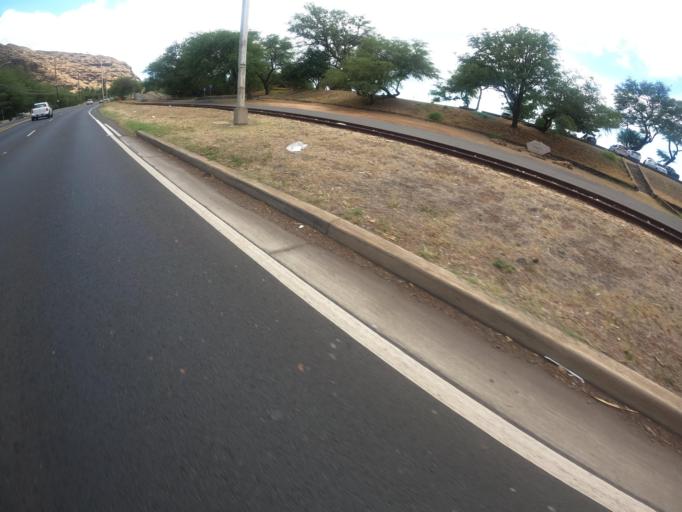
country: US
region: Hawaii
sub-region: Honolulu County
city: Nanakuli
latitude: 21.3775
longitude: -158.1411
